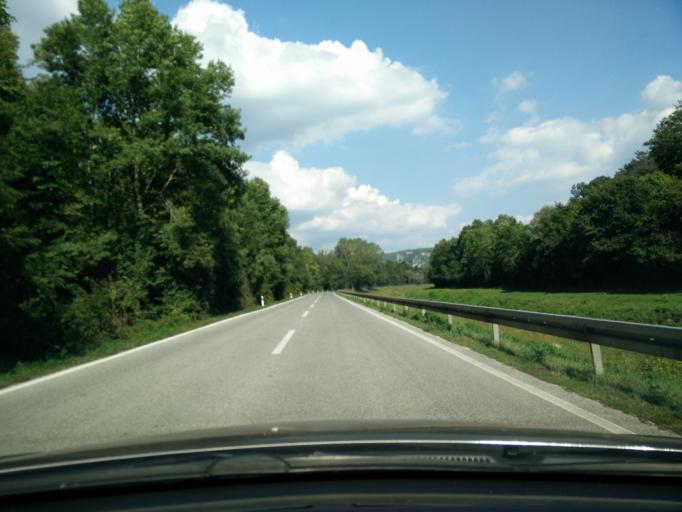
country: HR
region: Istarska
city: Karojba
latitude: 45.3628
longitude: 13.8651
